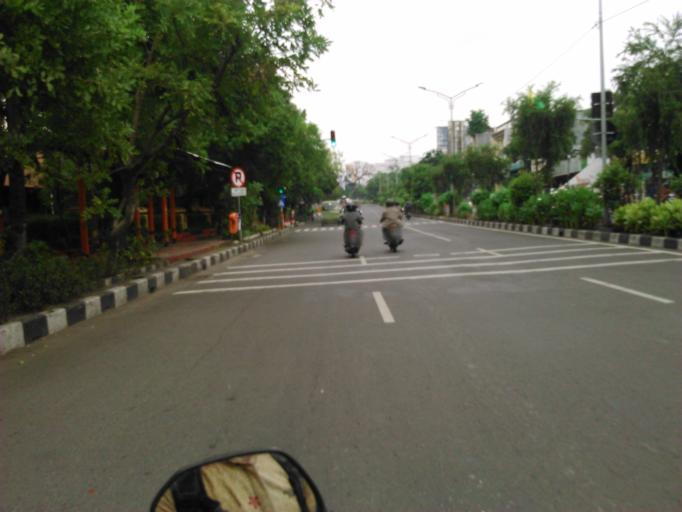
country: ID
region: East Java
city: Gubengairlangga
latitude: -7.2656
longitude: 112.7557
